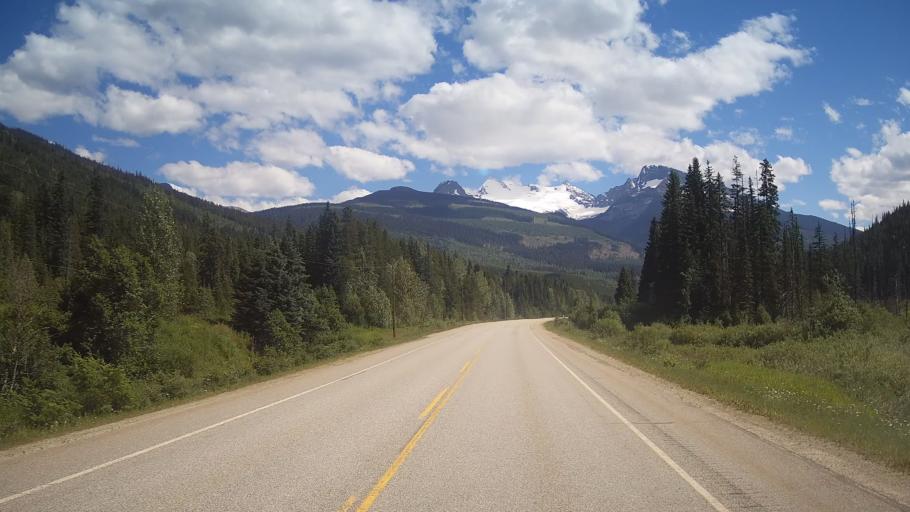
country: CA
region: Alberta
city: Jasper Park Lodge
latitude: 52.5963
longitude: -119.1033
